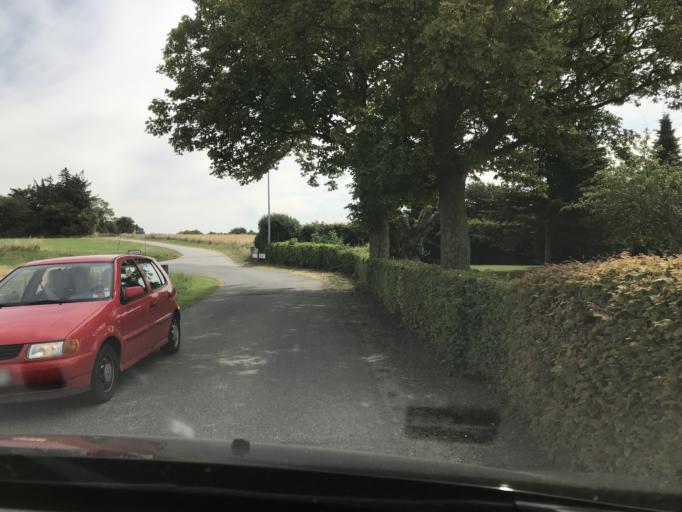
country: DK
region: South Denmark
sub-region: AEro Kommune
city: AEroskobing
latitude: 54.9133
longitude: 10.2696
